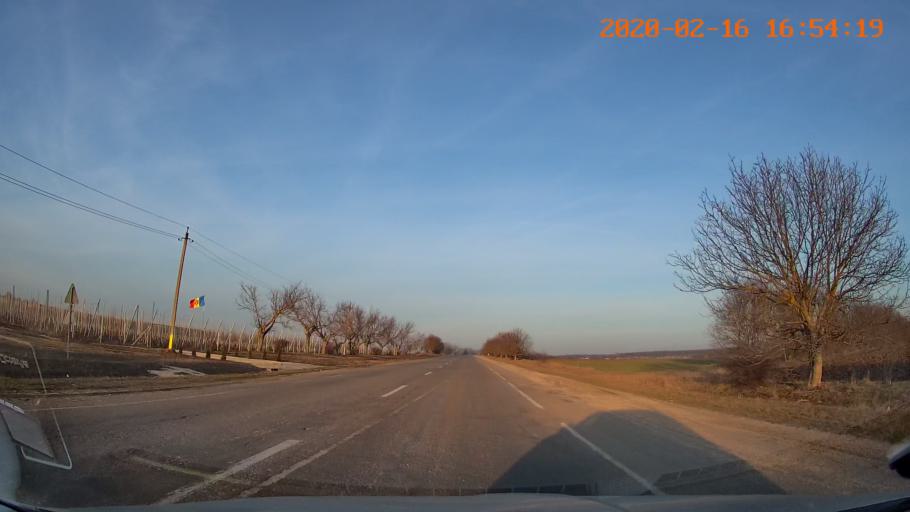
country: MD
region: Briceni
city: Briceni
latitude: 48.3196
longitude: 27.0046
